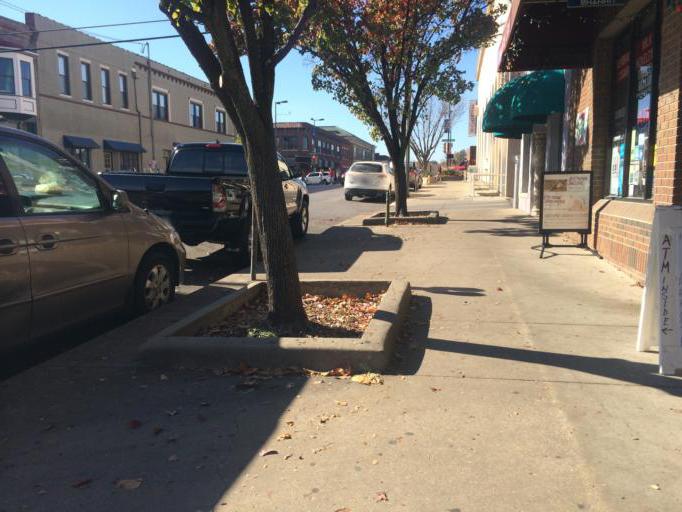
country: US
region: Kansas
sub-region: Douglas County
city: Lawrence
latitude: 38.9694
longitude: -95.2349
